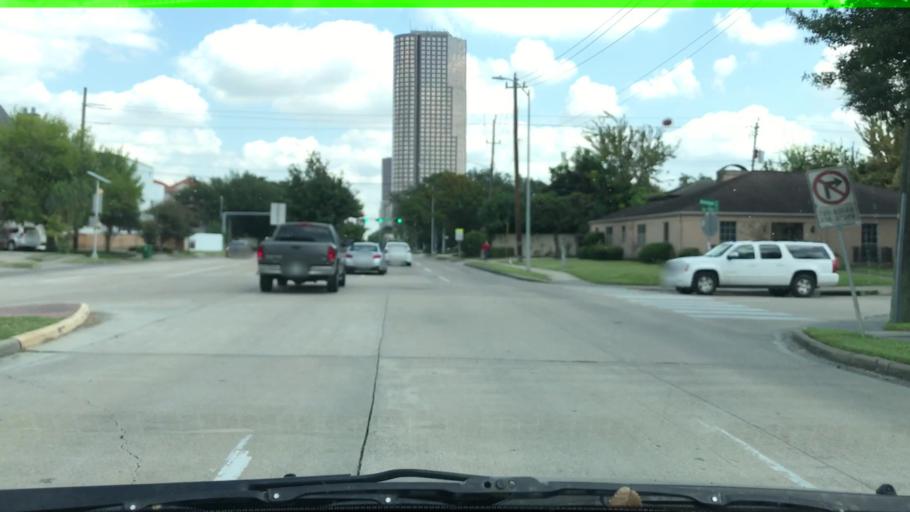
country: US
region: Texas
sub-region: Harris County
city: Hunters Creek Village
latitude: 29.7498
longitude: -95.4901
